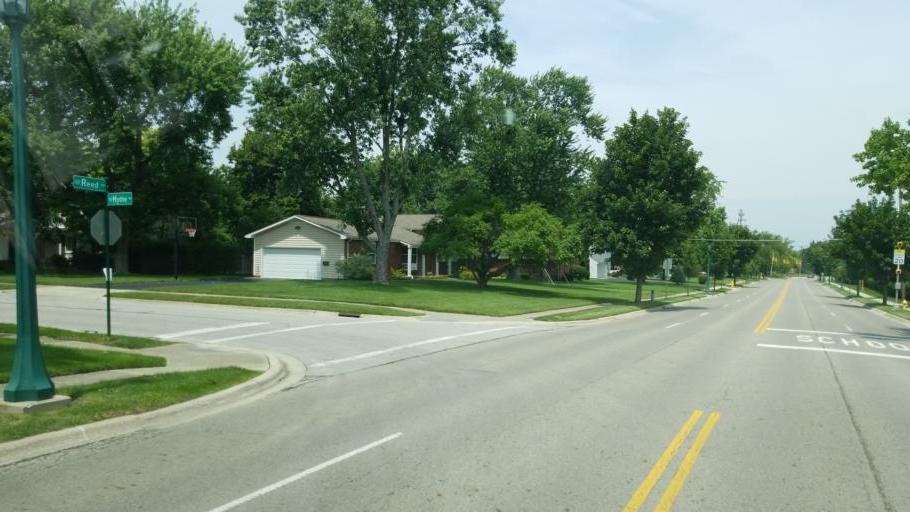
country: US
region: Ohio
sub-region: Franklin County
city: Upper Arlington
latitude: 40.0303
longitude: -83.0657
